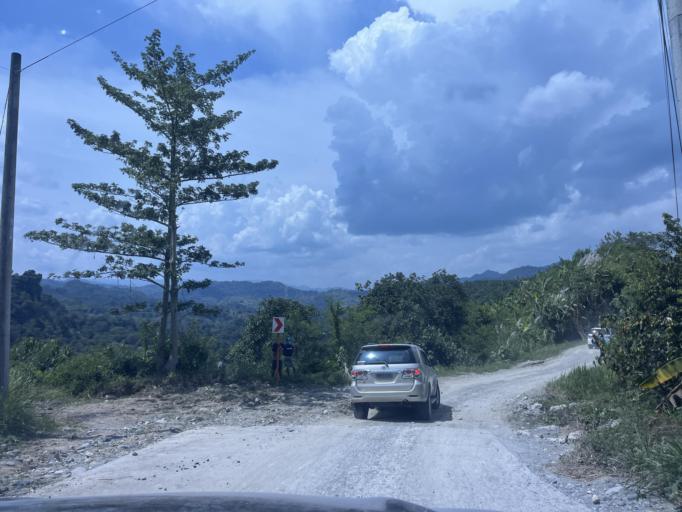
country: PH
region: Davao
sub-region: Province of Davao del Sur
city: Tamugan
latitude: 7.2868
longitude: 125.3382
